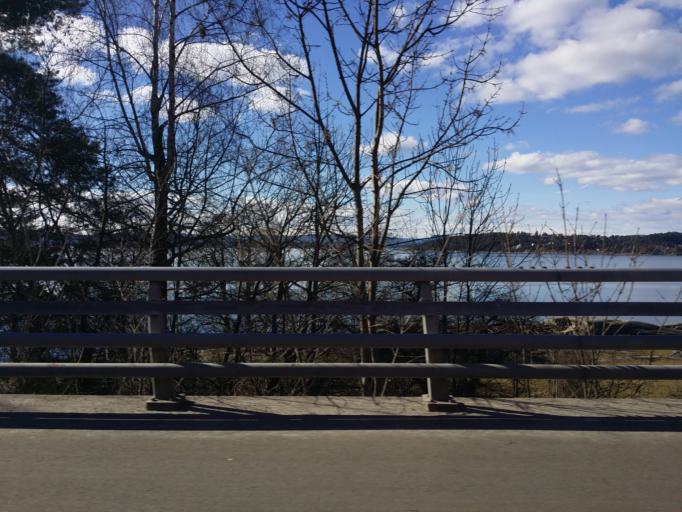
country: NO
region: Akershus
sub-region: Oppegard
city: Kolbotn
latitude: 59.8546
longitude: 10.7840
